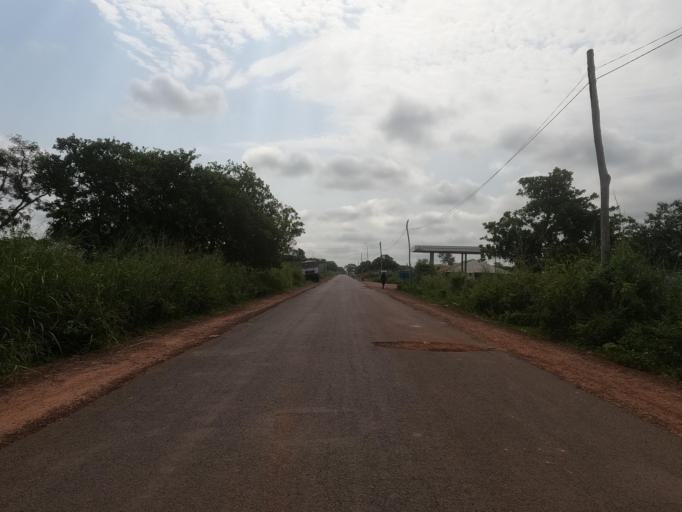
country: SN
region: Ziguinchor
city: Adeane
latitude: 12.3985
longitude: -15.7897
